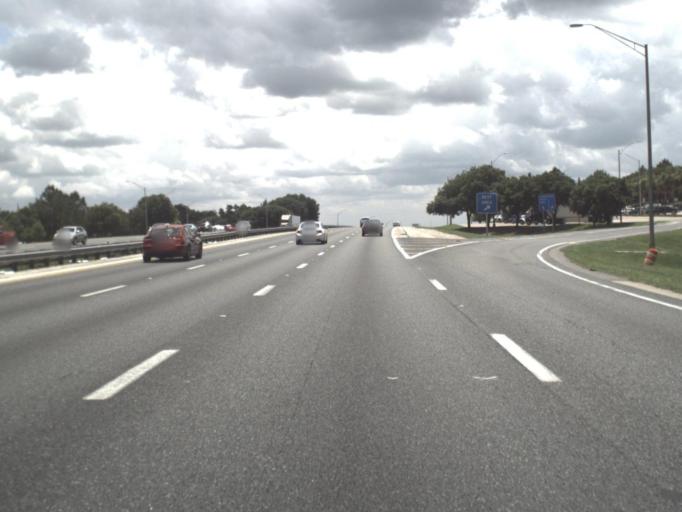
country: US
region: Florida
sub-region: Alachua County
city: Gainesville
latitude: 29.5921
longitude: -82.3646
